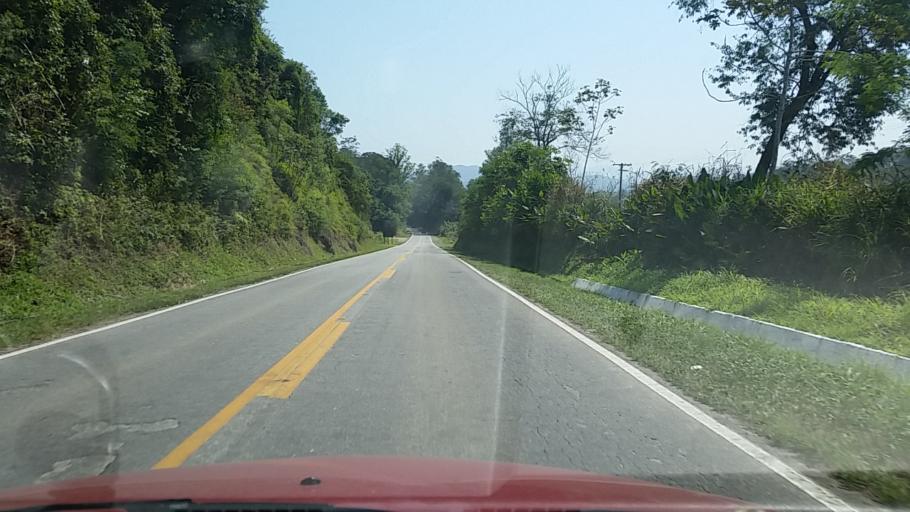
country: BR
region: Sao Paulo
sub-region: Miracatu
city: Miracatu
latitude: -24.3233
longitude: -47.5086
